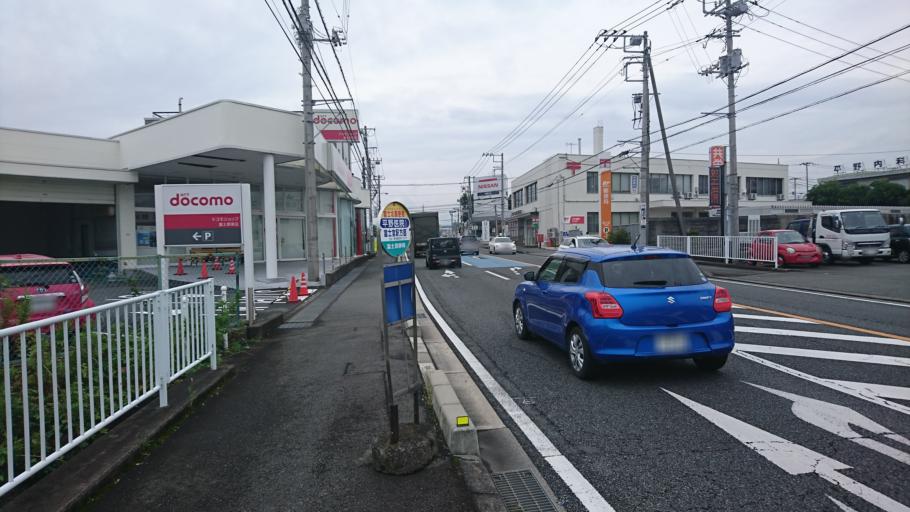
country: JP
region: Shizuoka
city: Fuji
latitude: 35.1870
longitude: 138.6537
